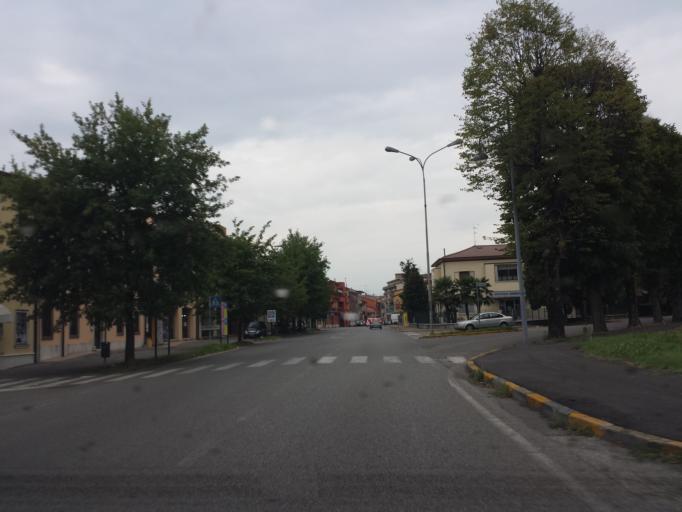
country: IT
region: Veneto
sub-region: Provincia di Verona
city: San Bonifacio
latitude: 45.3928
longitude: 11.2750
